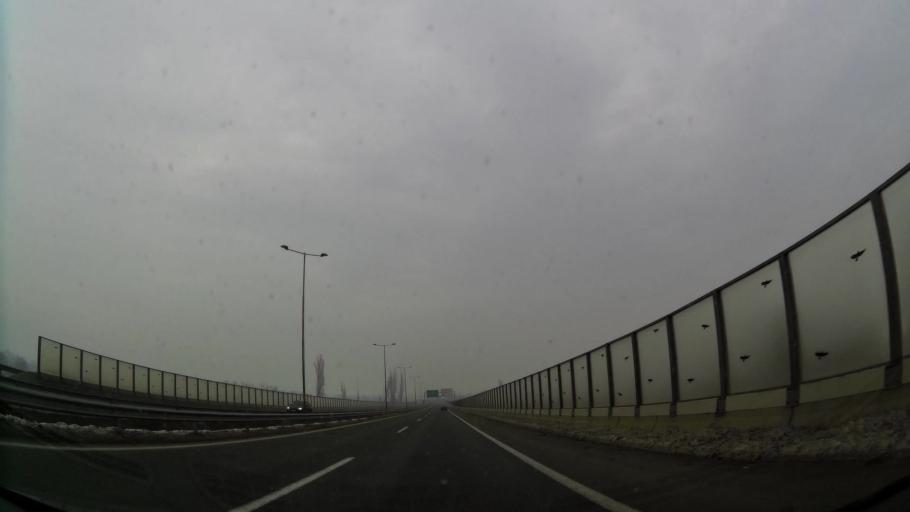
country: MK
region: Cucer-Sandevo
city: Chucher - Sandevo
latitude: 42.0550
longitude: 21.3577
